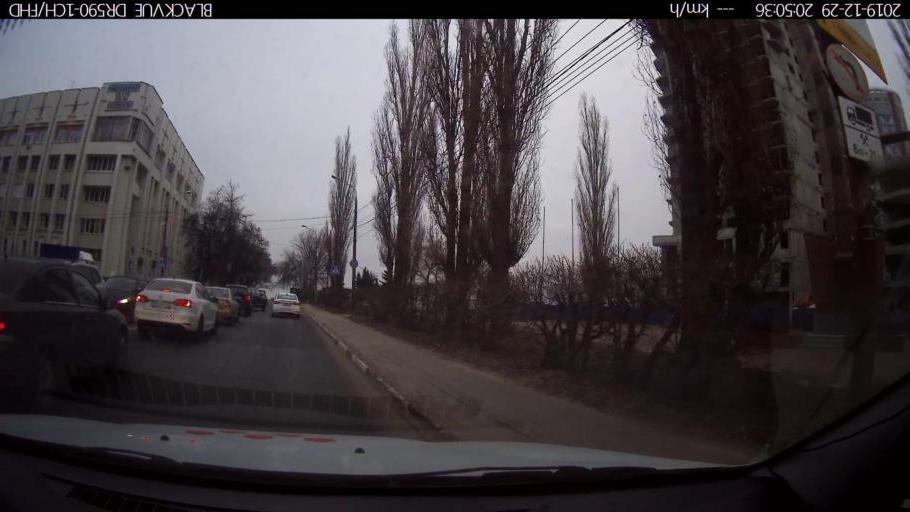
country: RU
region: Nizjnij Novgorod
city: Nizhniy Novgorod
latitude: 56.3176
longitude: 44.0320
